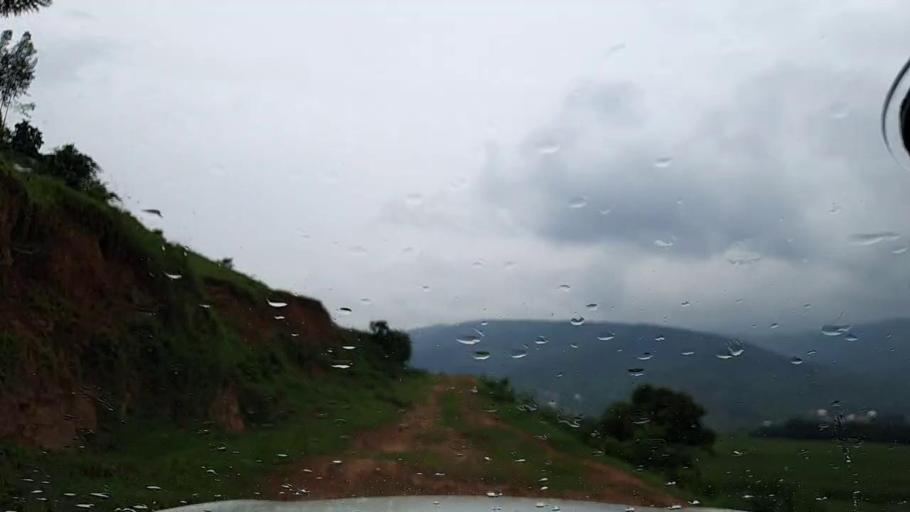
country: RW
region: Kigali
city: Kigali
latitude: -1.9078
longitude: 29.9581
